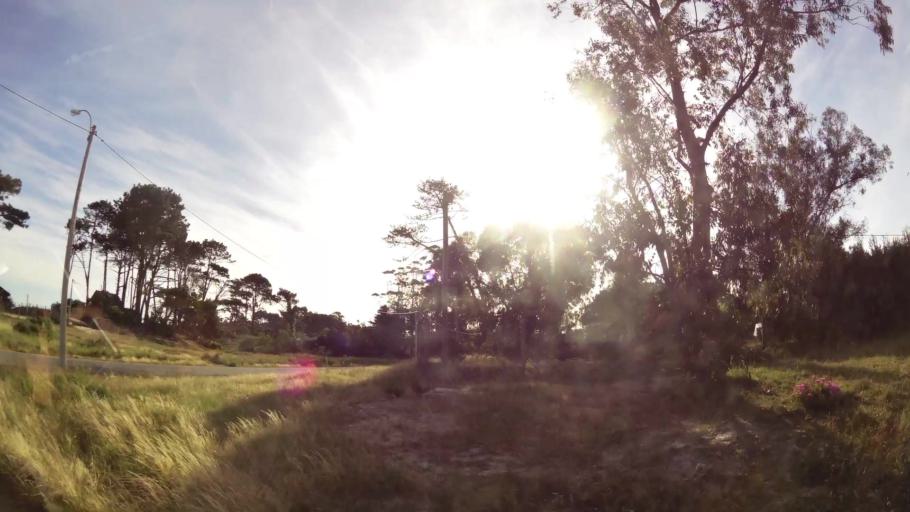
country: UY
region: Canelones
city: Atlantida
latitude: -34.7899
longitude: -55.8529
